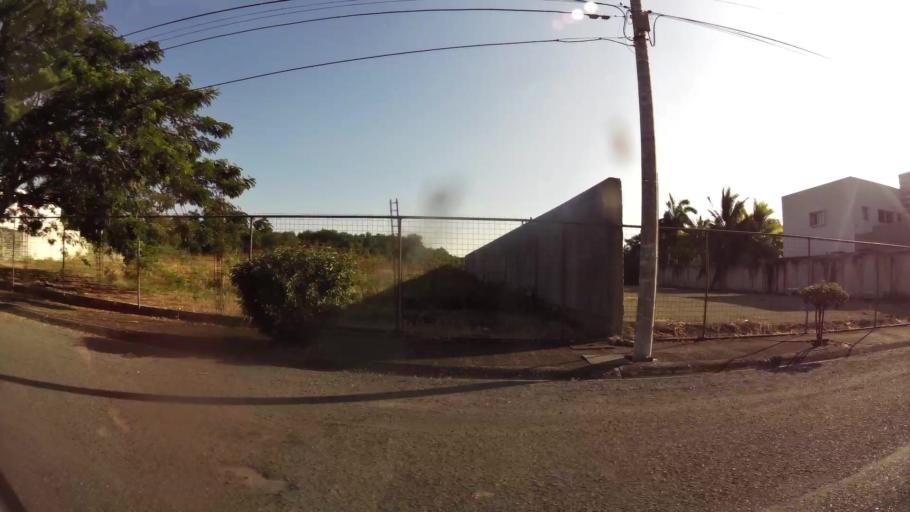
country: EC
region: Guayas
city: Santa Lucia
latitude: -2.1947
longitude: -79.9710
